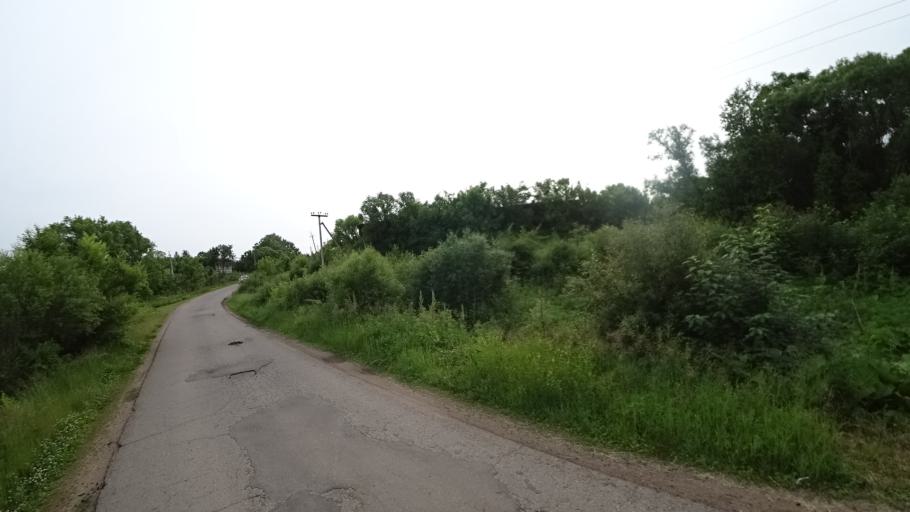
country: RU
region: Primorskiy
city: Novosysoyevka
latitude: 44.2453
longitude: 133.3702
